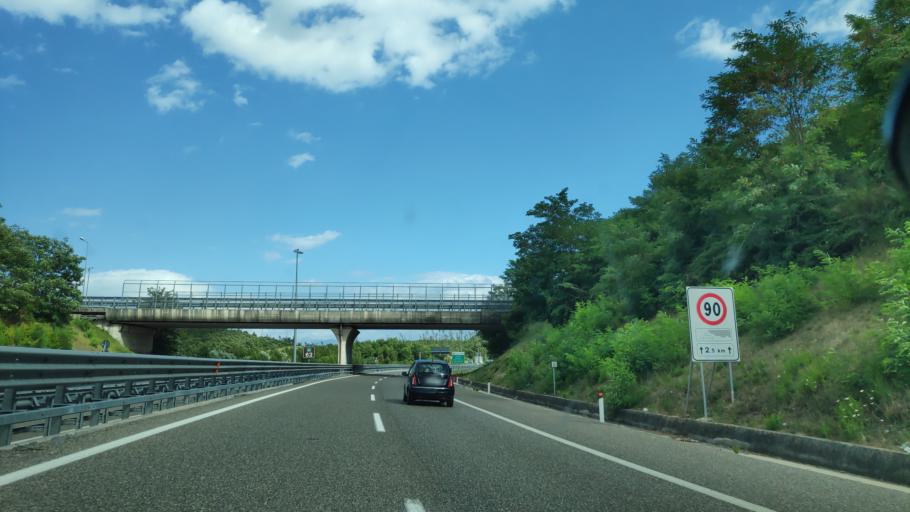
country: IT
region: Campania
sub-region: Provincia di Salerno
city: Sicignano degli Alburni
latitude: 40.6094
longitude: 15.2948
